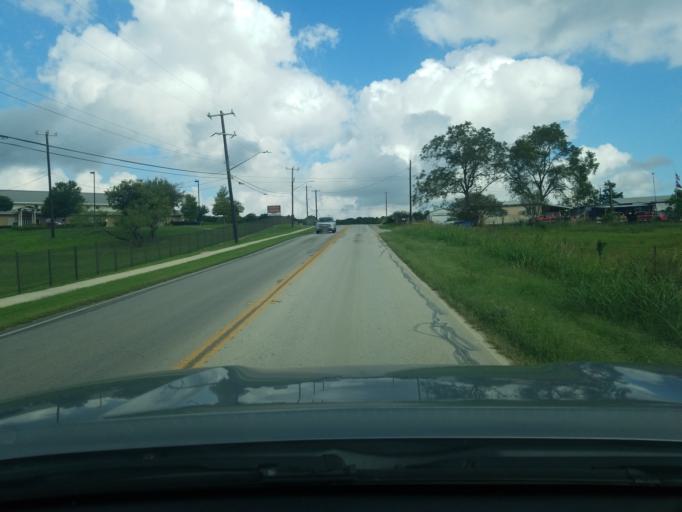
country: US
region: Texas
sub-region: Bexar County
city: Live Oak
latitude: 29.5807
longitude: -98.3637
